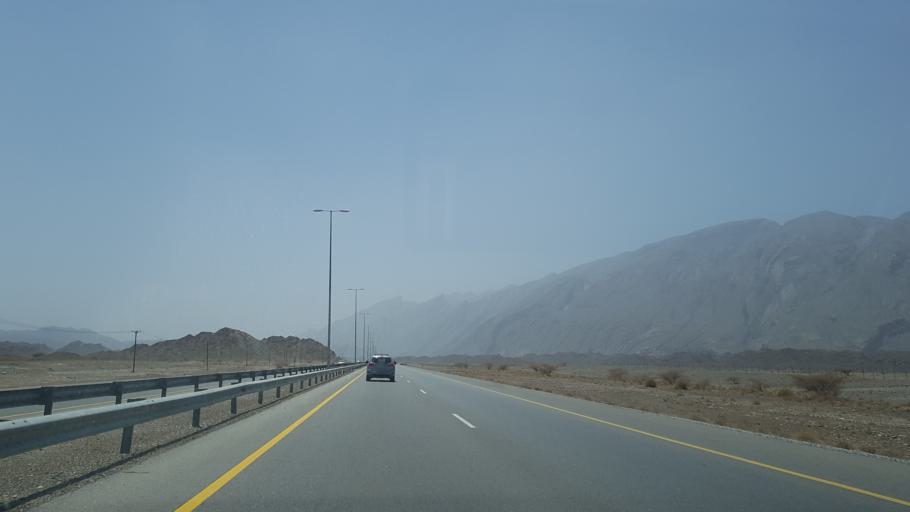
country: OM
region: Muhafazat ad Dakhiliyah
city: Sufalat Sama'il
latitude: 23.2430
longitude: 57.9154
